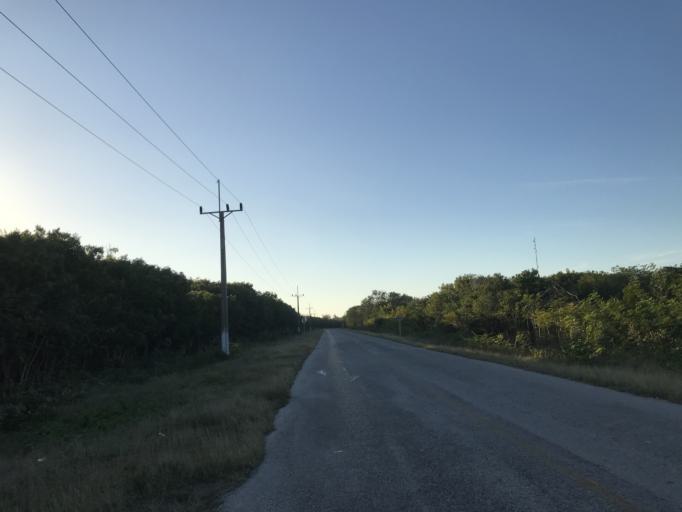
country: CU
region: Cienfuegos
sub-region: Municipio de Aguada de Pasajeros
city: Aguada de Pasajeros
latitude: 22.0670
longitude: -81.0442
